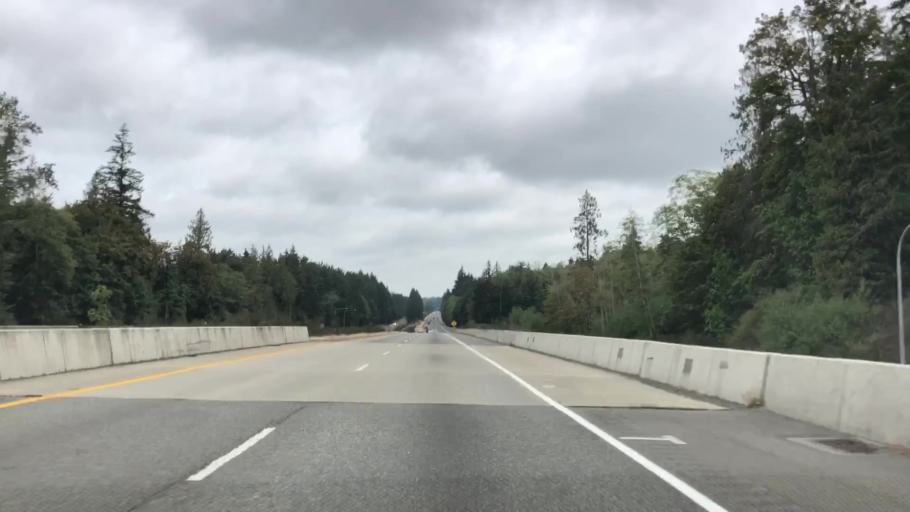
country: US
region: Washington
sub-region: Kitsap County
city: Burley
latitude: 47.4322
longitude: -122.6229
